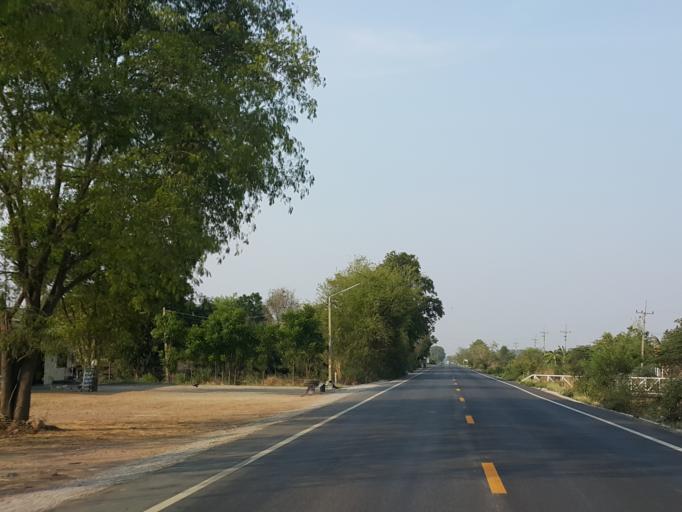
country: TH
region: Chai Nat
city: Sankhaburi
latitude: 14.9888
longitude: 100.1127
